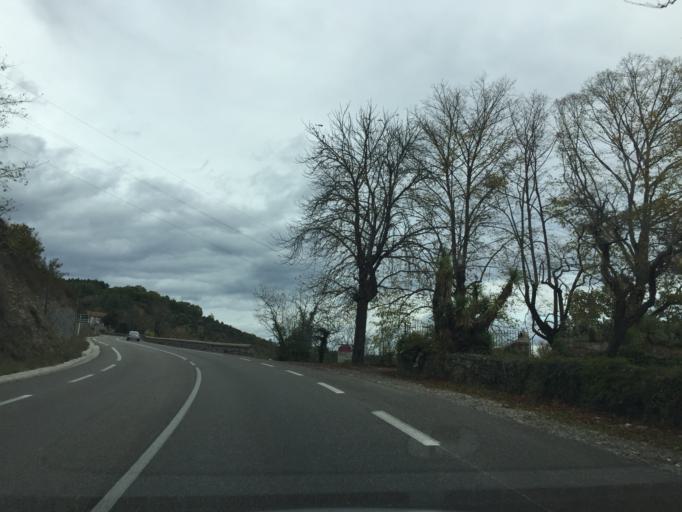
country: FR
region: Rhone-Alpes
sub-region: Departement de l'Ardeche
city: Largentiere
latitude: 44.5093
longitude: 4.3167
